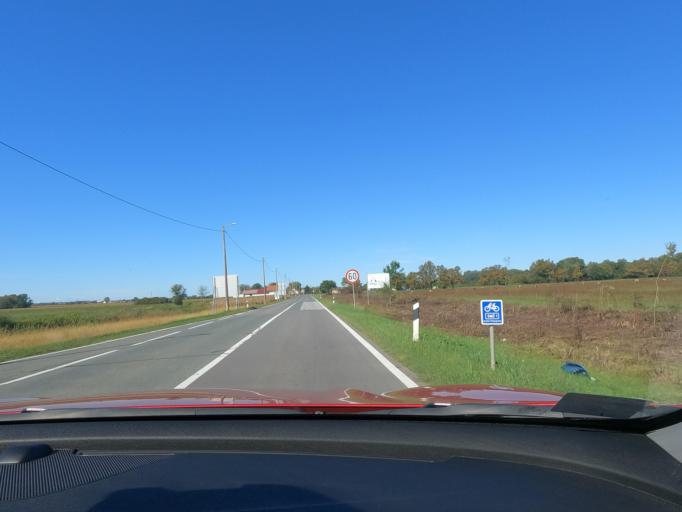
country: HR
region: Sisacko-Moslavacka
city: Budasevo
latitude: 45.4863
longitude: 16.4661
